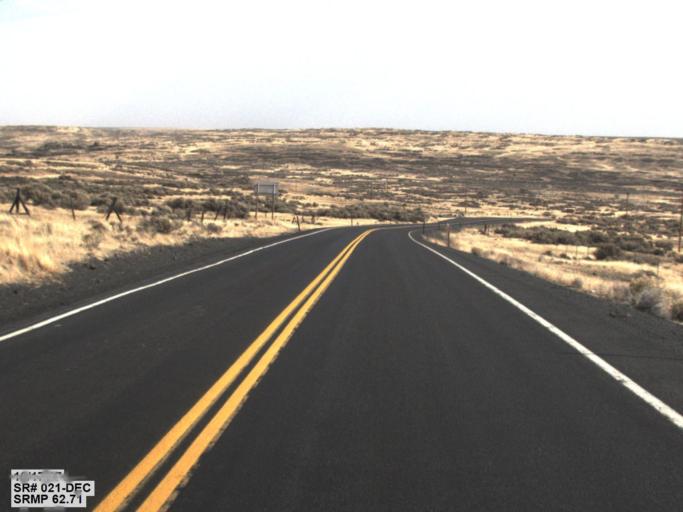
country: US
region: Washington
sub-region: Adams County
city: Ritzville
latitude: 47.4219
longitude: -118.6950
